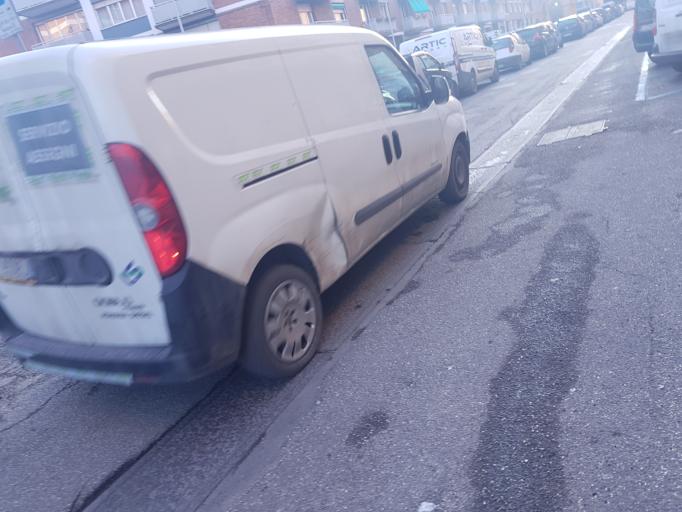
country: IT
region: Emilia-Romagna
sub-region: Provincia di Bologna
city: Bologna
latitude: 44.5035
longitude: 11.3388
